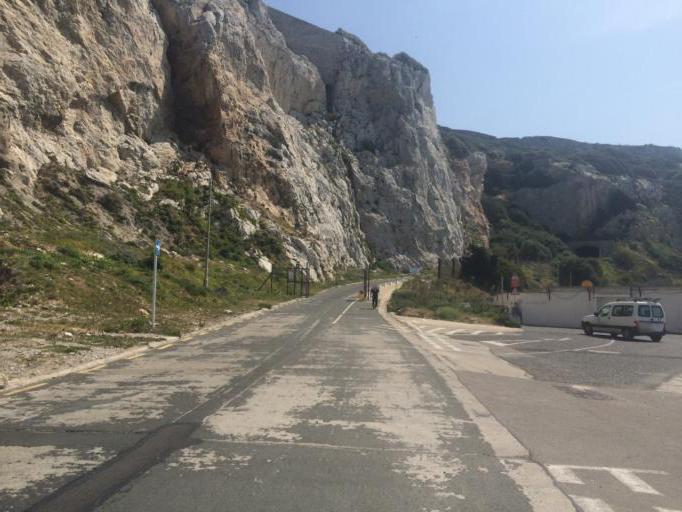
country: GI
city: Gibraltar
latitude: 36.1169
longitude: -5.3499
